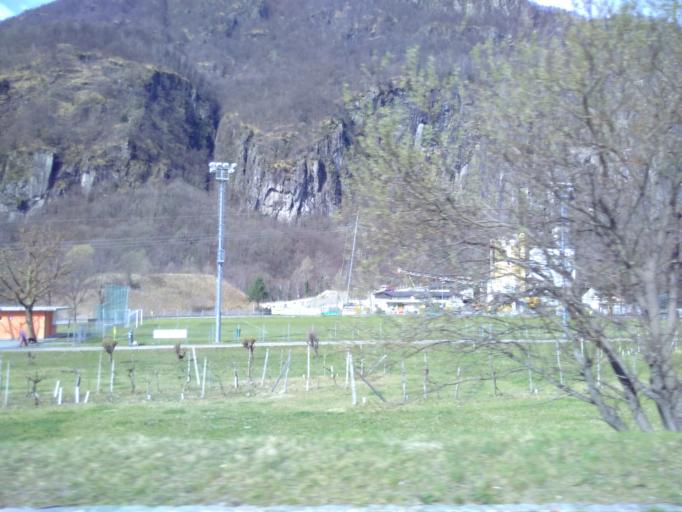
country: CH
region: Ticino
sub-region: Locarno District
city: Verscio
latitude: 46.2089
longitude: 8.7437
